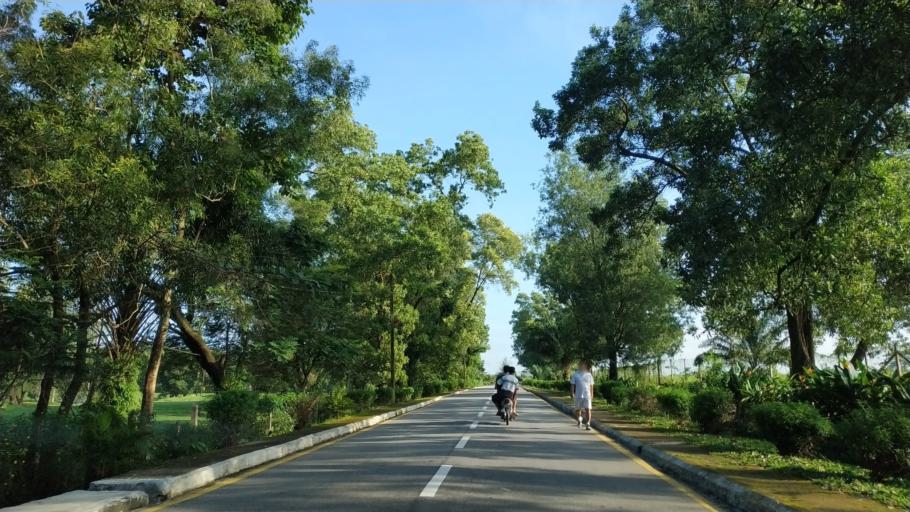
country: MM
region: Tanintharyi
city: Dawei
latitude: 14.0895
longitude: 98.2082
